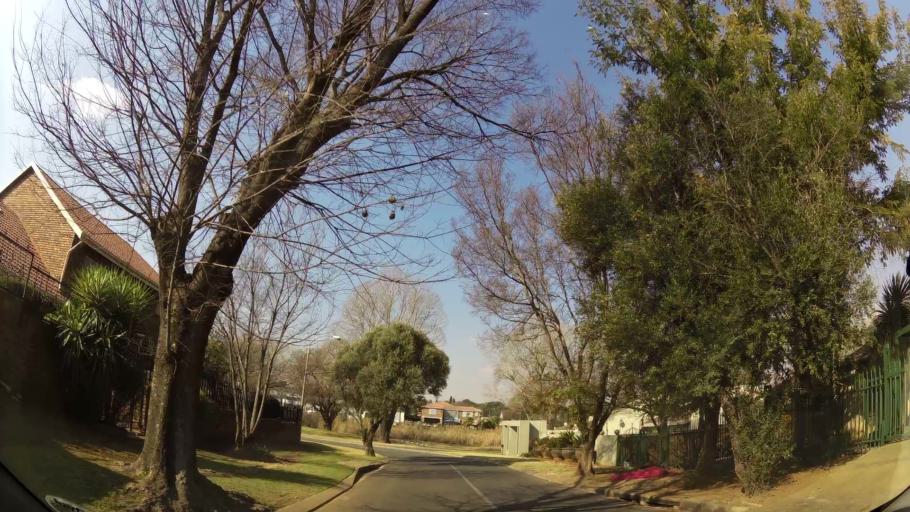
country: ZA
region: Gauteng
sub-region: Ekurhuleni Metropolitan Municipality
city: Benoni
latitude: -26.1548
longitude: 28.2873
